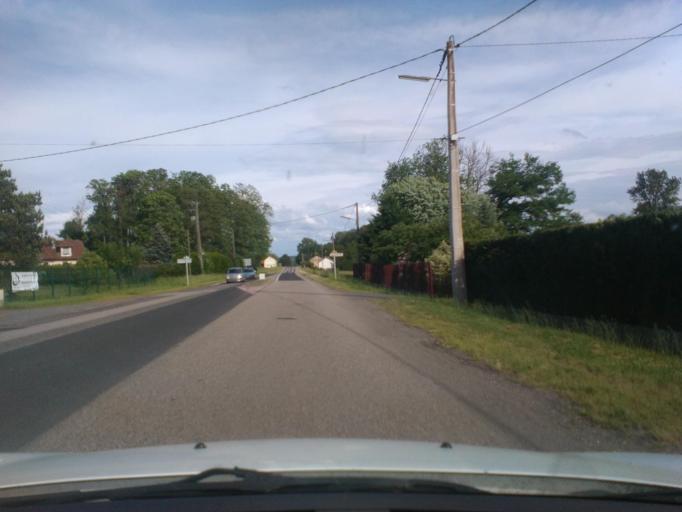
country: FR
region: Lorraine
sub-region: Departement de Meurthe-et-Moselle
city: Baccarat
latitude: 48.4827
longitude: 6.7021
